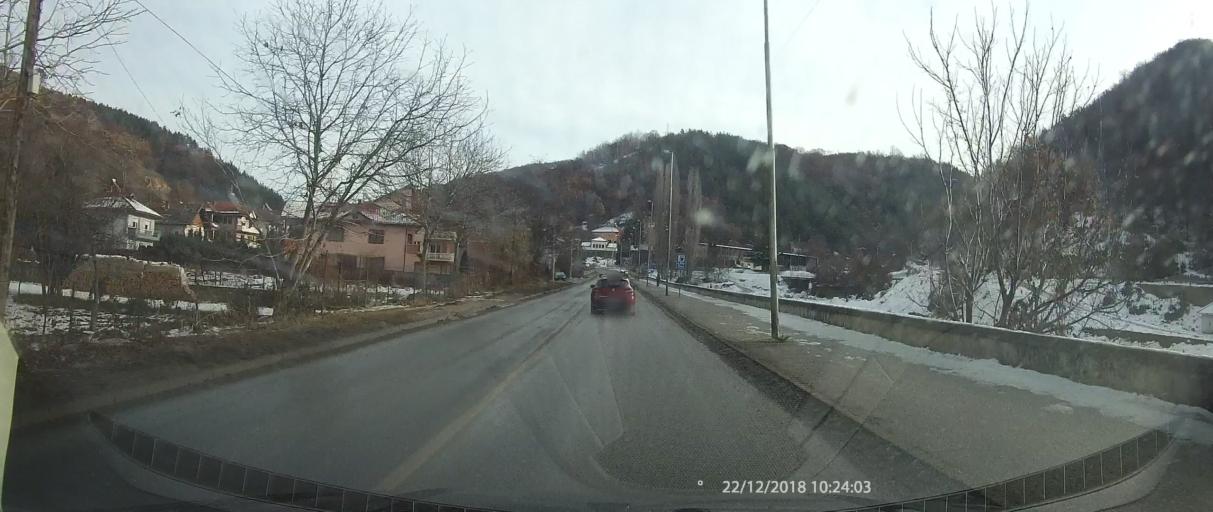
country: MK
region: Kriva Palanka
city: Kriva Palanka
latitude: 42.2117
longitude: 22.3430
